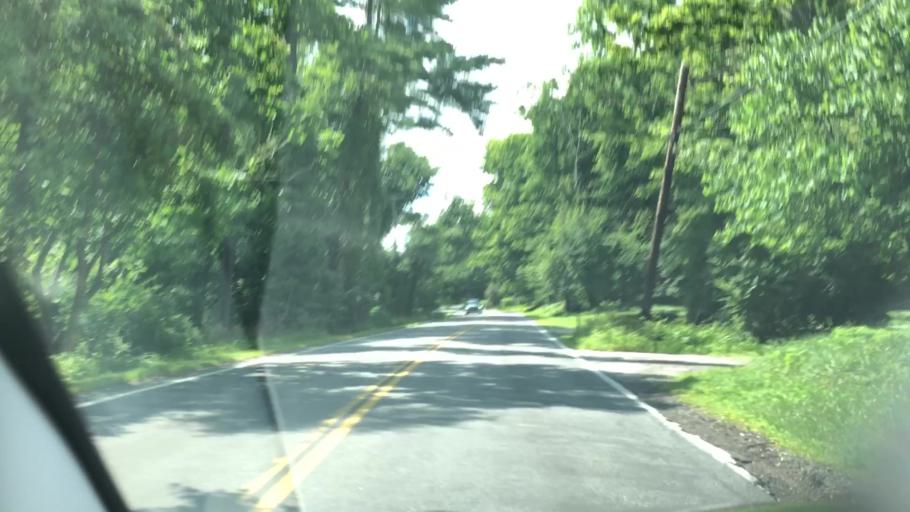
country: US
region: Ohio
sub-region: Summit County
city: Montrose-Ghent
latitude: 41.1600
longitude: -81.6468
